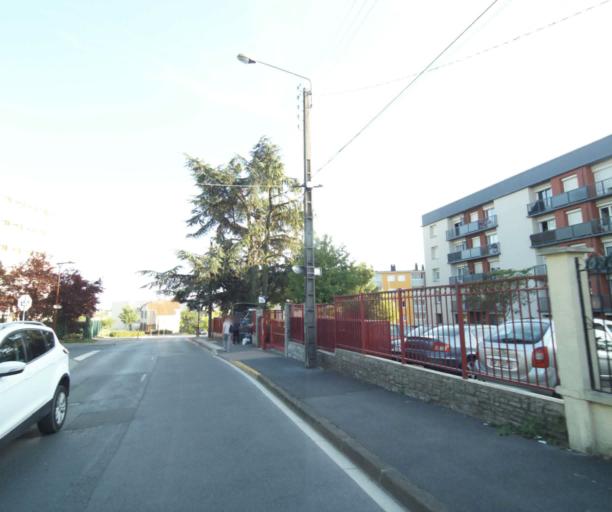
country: FR
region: Champagne-Ardenne
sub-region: Departement des Ardennes
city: Charleville-Mezieres
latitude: 49.7839
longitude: 4.7095
